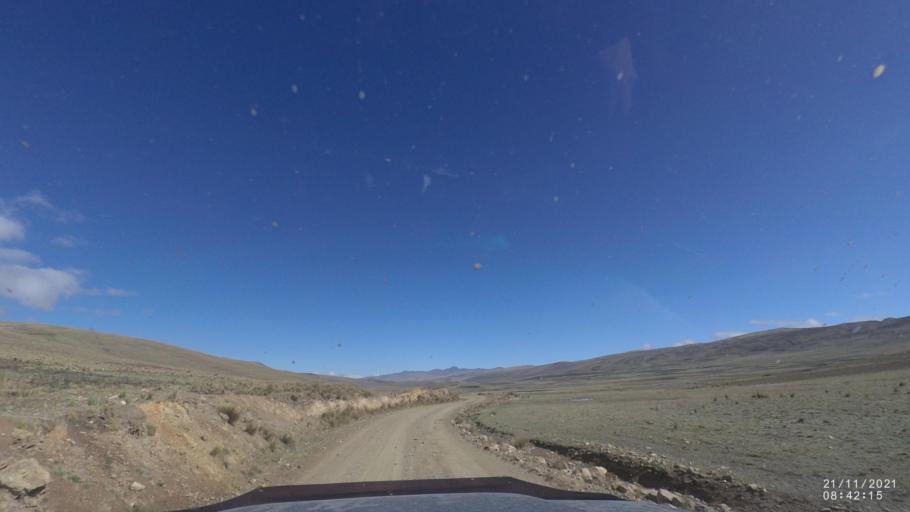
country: BO
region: Cochabamba
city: Cochabamba
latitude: -17.2673
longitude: -66.2206
